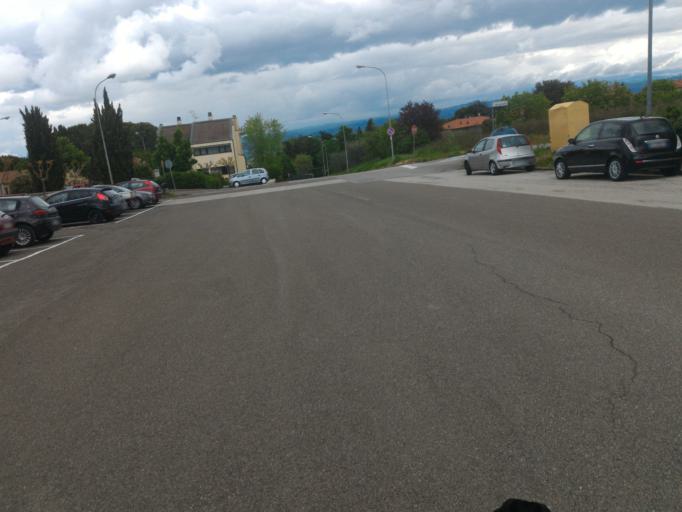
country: IT
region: Tuscany
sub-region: Province of Florence
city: Gambassi Terme
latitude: 43.5322
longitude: 10.9503
